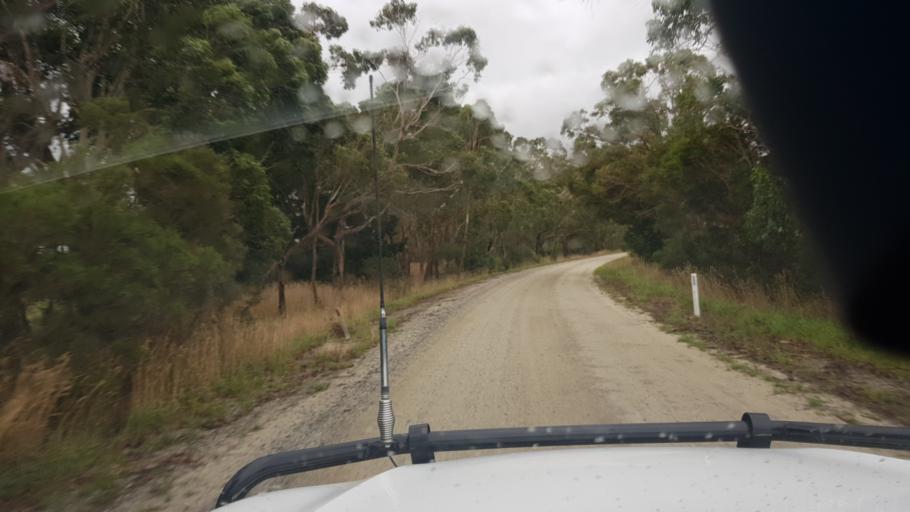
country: AU
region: Victoria
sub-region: Cardinia
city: Bunyip
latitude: -38.0862
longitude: 145.7611
